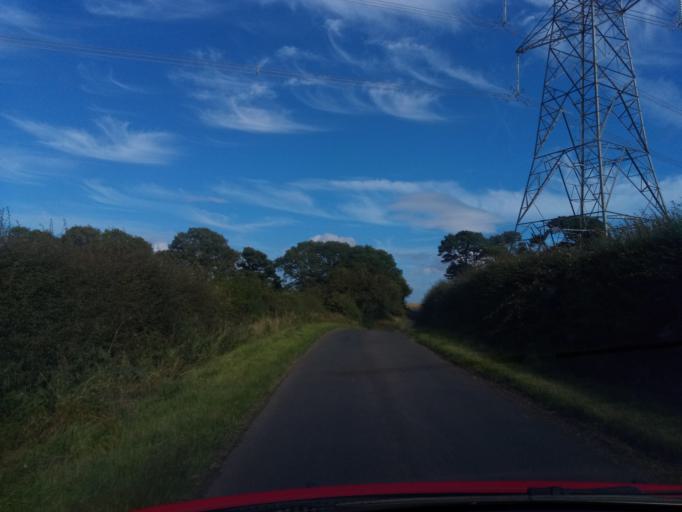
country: GB
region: Scotland
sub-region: The Scottish Borders
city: Coldstream
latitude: 55.6177
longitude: -2.1790
